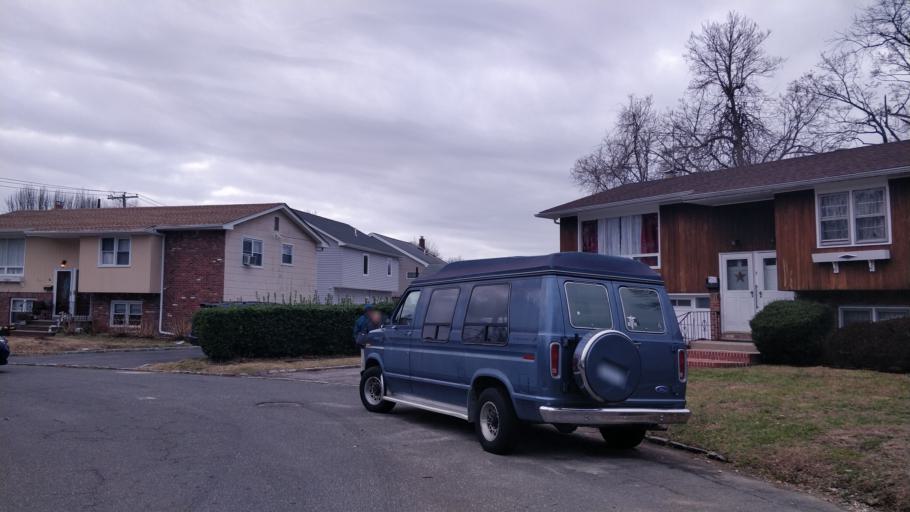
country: US
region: New York
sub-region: Nassau County
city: Glen Cove
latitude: 40.8727
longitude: -73.6324
